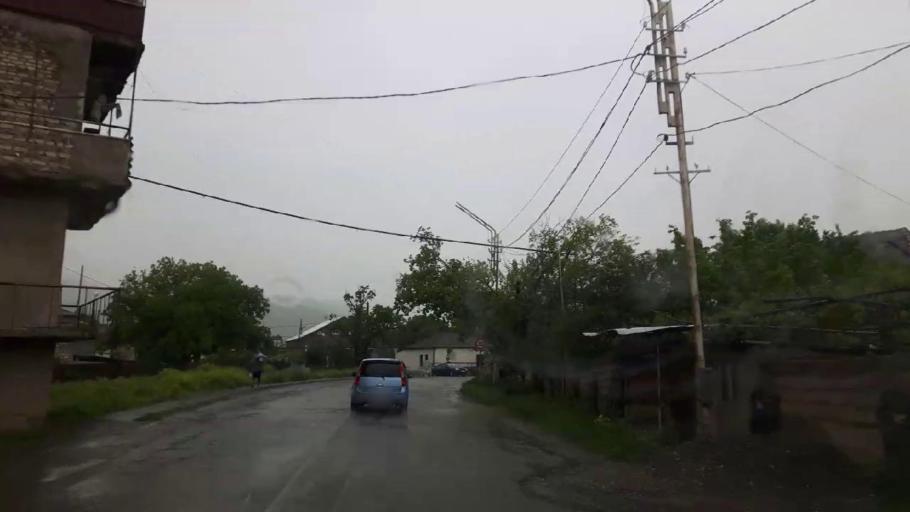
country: GE
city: Agara
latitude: 42.0179
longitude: 43.8837
